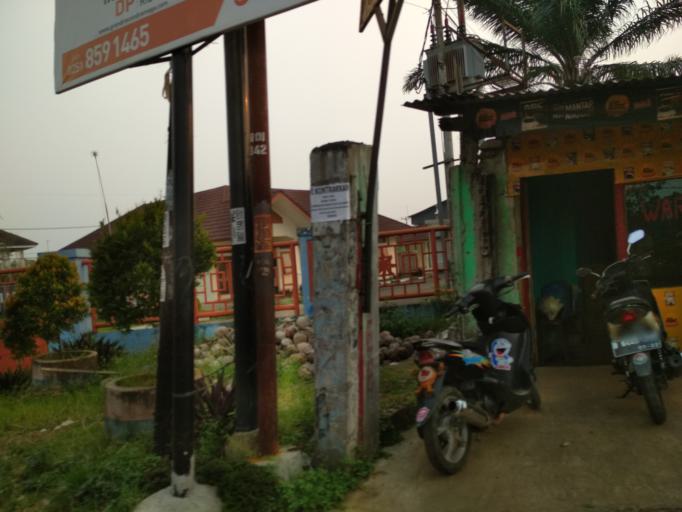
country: ID
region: West Java
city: Ciampea
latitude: -6.5645
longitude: 106.7343
